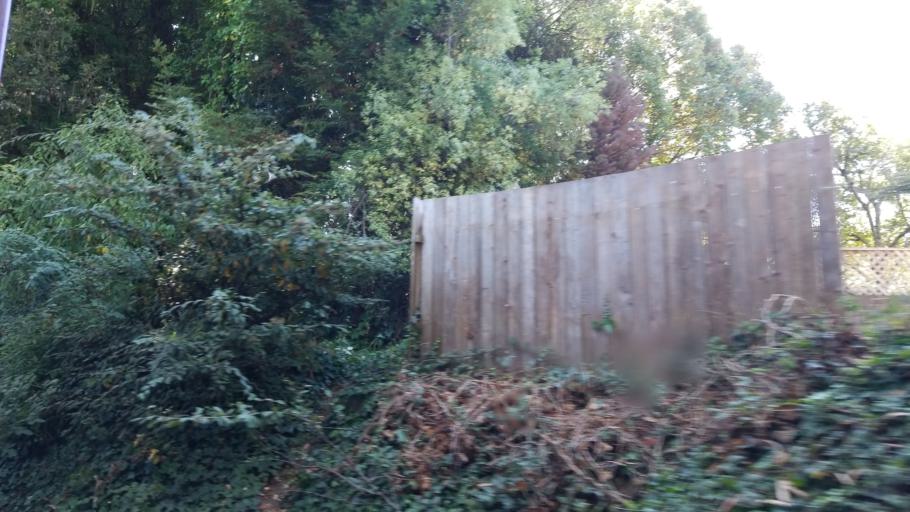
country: US
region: California
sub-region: Mendocino County
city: Fort Bragg
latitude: 39.4512
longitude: -123.8008
